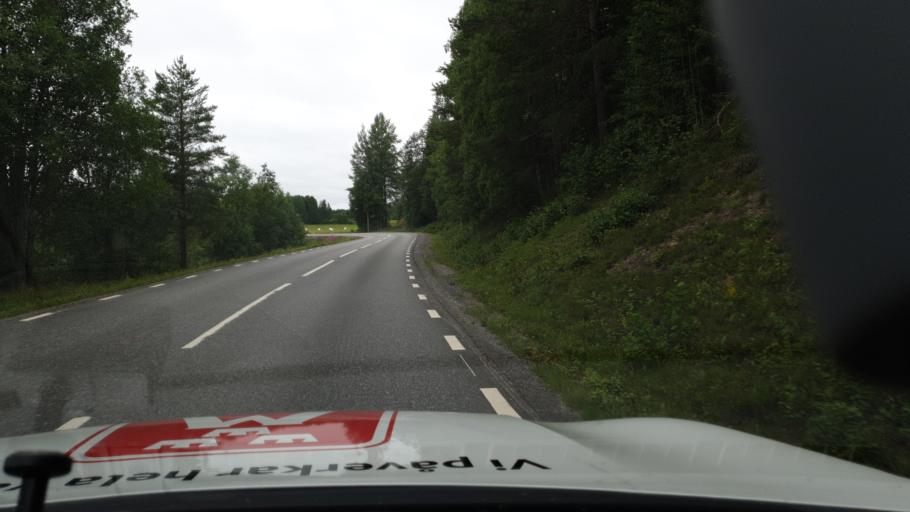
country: SE
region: Vaesterbotten
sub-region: Umea Kommun
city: Ersmark
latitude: 64.2491
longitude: 20.2574
